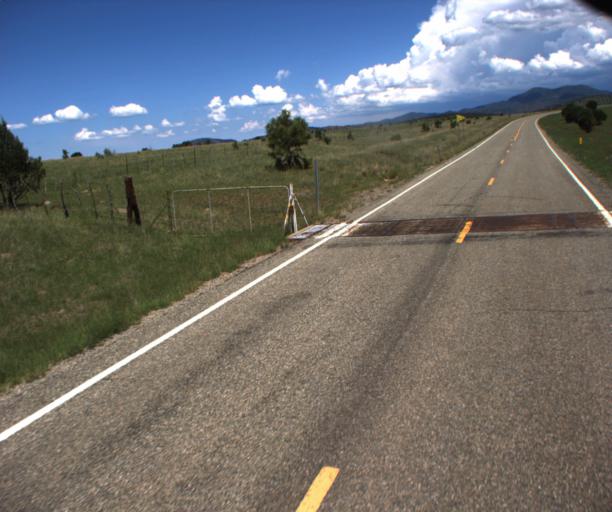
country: US
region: Arizona
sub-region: Greenlee County
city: Morenci
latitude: 33.3099
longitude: -109.3505
